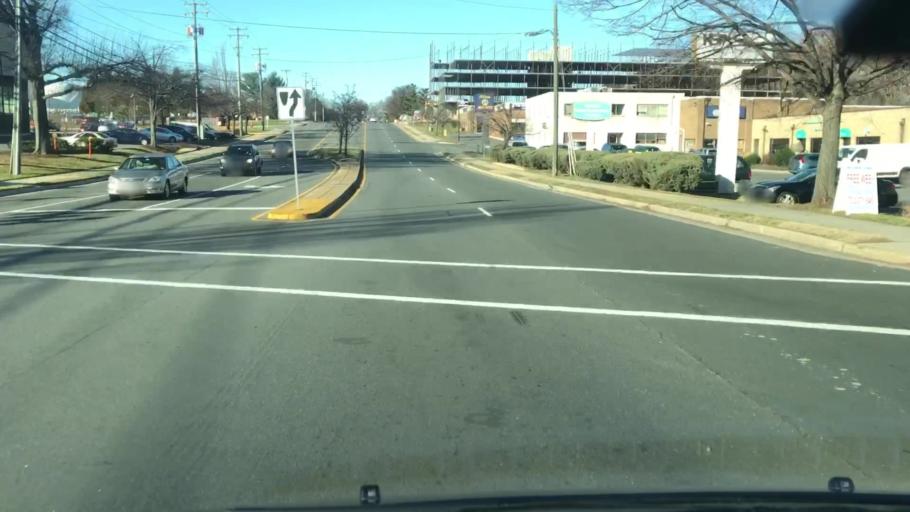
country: US
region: Virginia
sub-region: Fairfax County
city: Mantua
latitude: 38.8444
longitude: -77.2718
